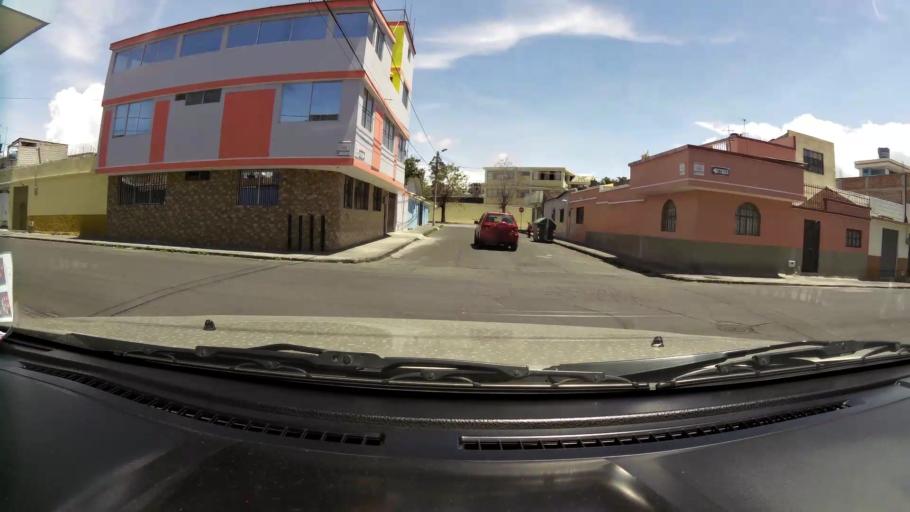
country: EC
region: Chimborazo
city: Riobamba
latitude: -1.6628
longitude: -78.6512
